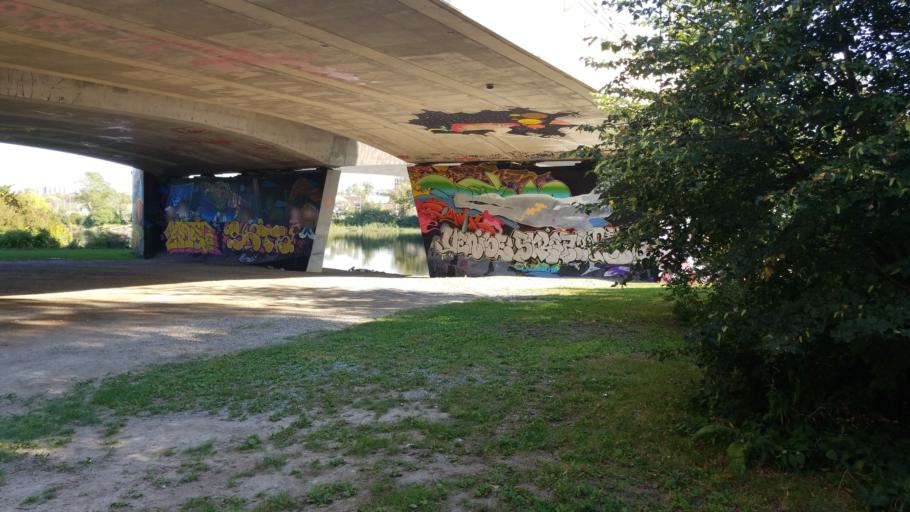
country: CA
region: Ontario
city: Ottawa
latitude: 45.3839
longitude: -75.6896
